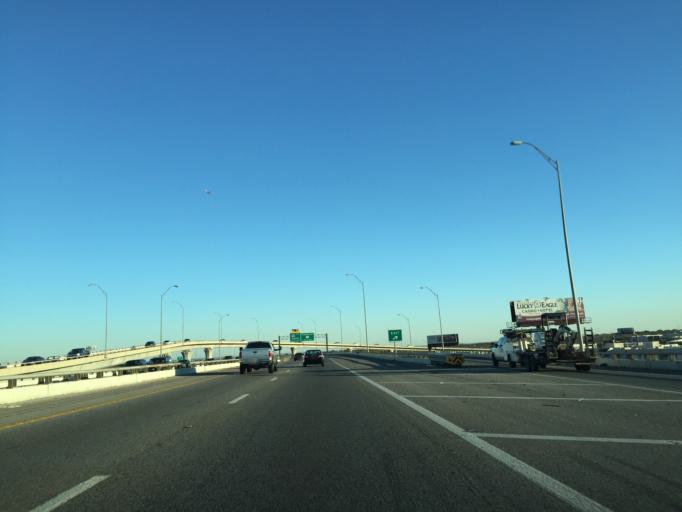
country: US
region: Texas
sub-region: Travis County
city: Austin
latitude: 30.3414
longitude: -97.7027
